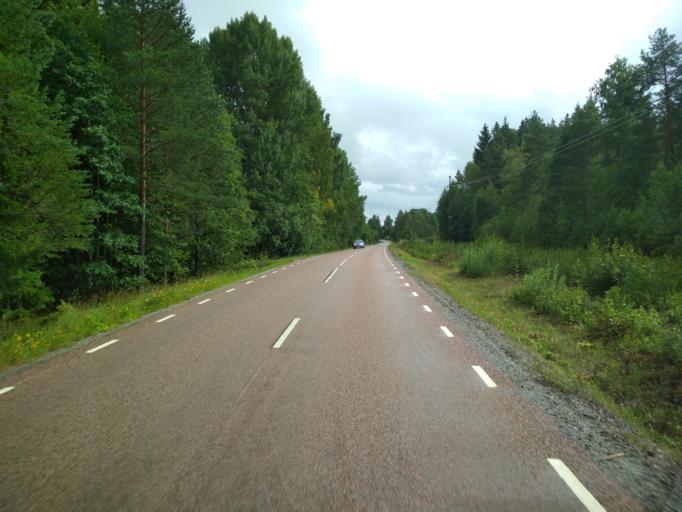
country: SE
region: Vaestmanland
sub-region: Surahammars Kommun
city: Ramnas
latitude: 59.8011
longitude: 16.1722
